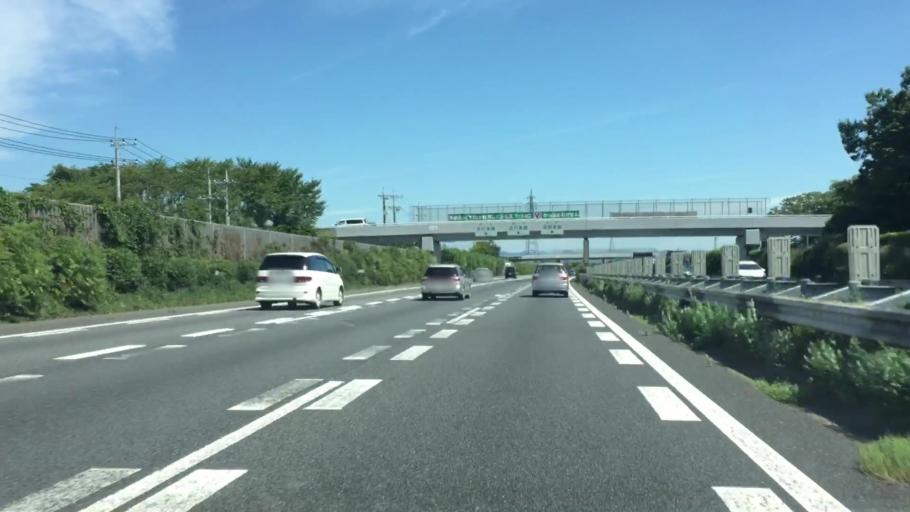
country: JP
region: Gunma
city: Tatebayashi
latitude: 36.2376
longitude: 139.5755
